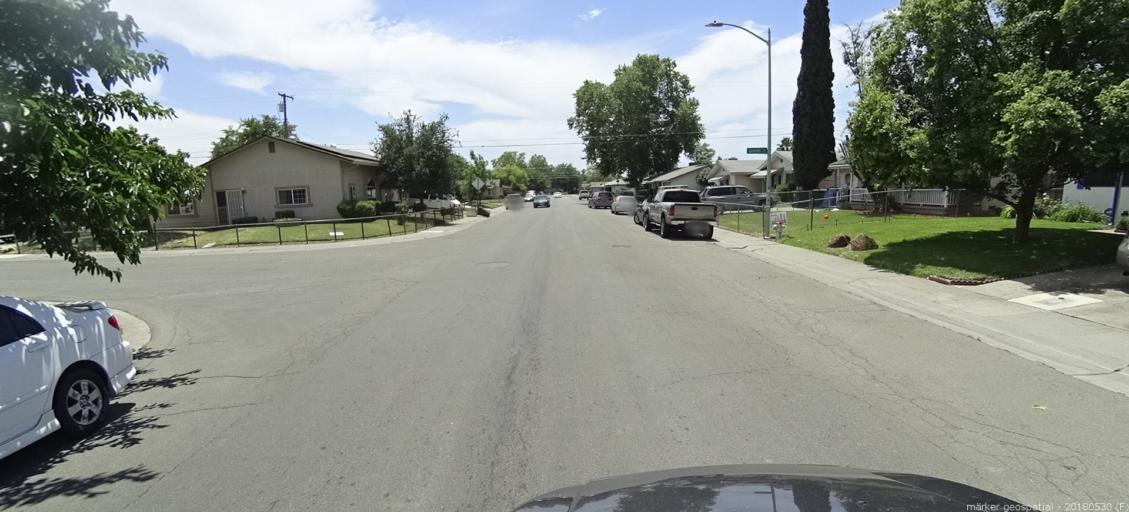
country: US
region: California
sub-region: Sacramento County
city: Sacramento
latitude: 38.6281
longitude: -121.4632
